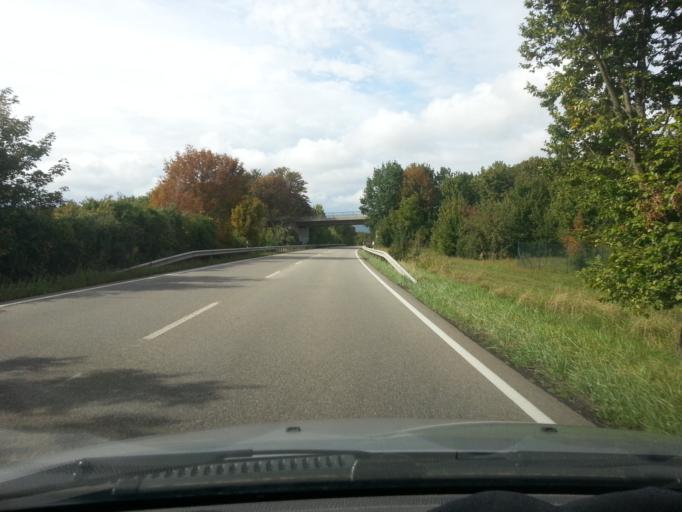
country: DE
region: Rheinland-Pfalz
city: Lachen-Speyerdorf
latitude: 49.3194
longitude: 8.1879
